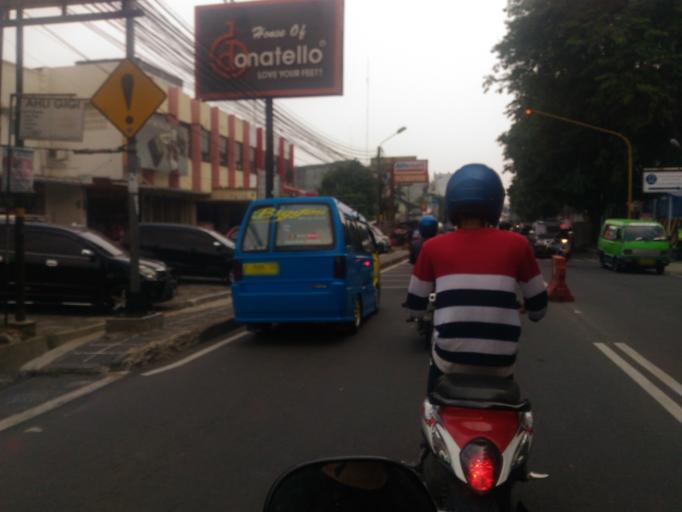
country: ID
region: West Java
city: Bogor
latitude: -6.6246
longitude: 106.8202
